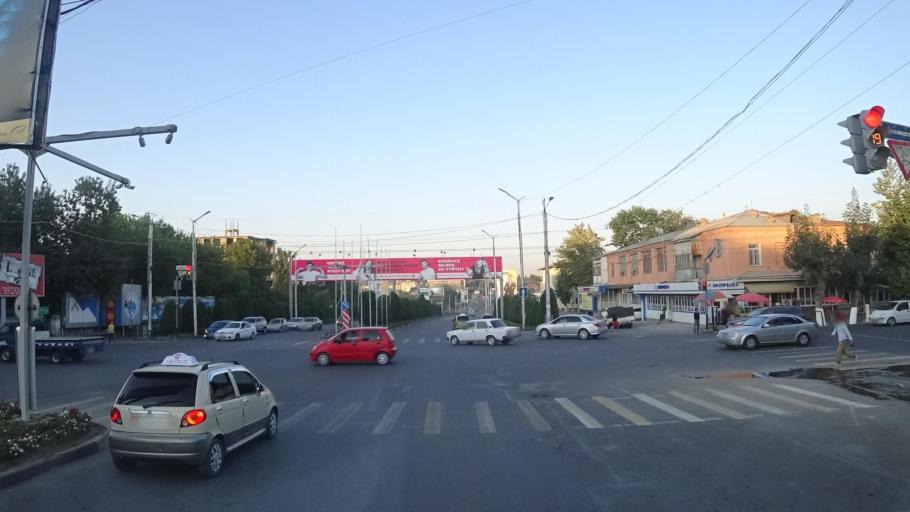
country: KG
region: Osh
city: Osh
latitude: 40.5250
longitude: 72.7981
